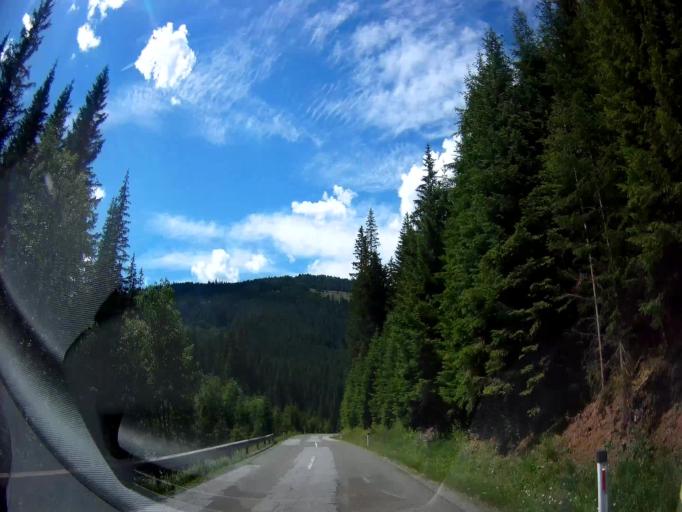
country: AT
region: Styria
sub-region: Politischer Bezirk Murau
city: Stadl an der Mur
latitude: 46.9757
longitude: 14.0088
